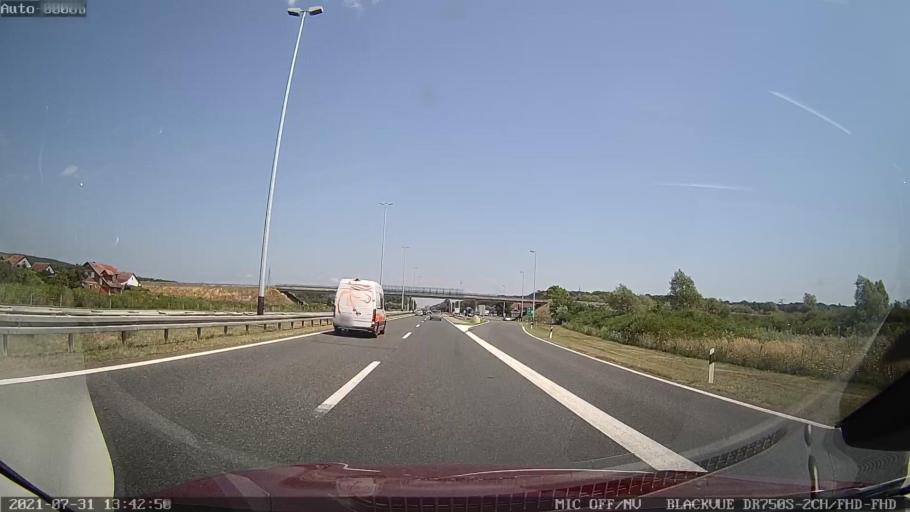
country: HR
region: Brodsko-Posavska
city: Oriovac
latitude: 45.1555
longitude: 17.8141
